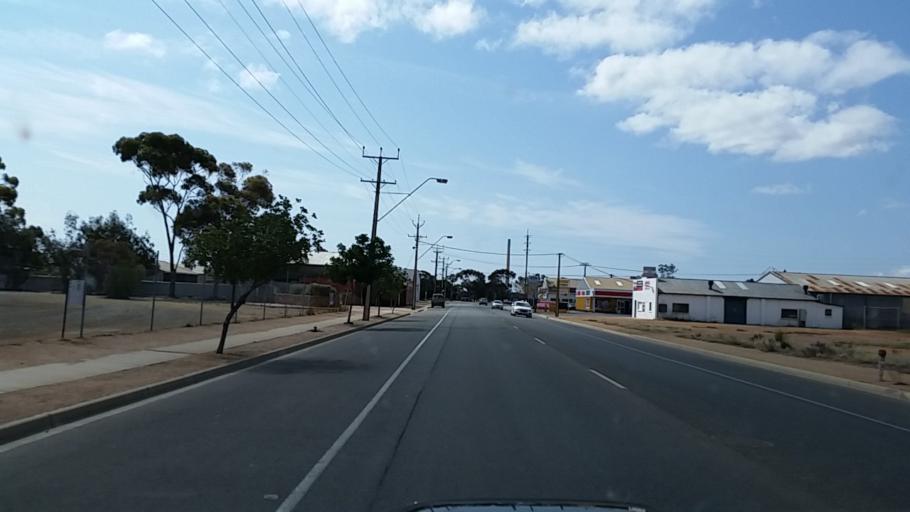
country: AU
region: South Australia
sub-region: Port Pirie City and Dists
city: Port Pirie
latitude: -33.1922
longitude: 138.0102
